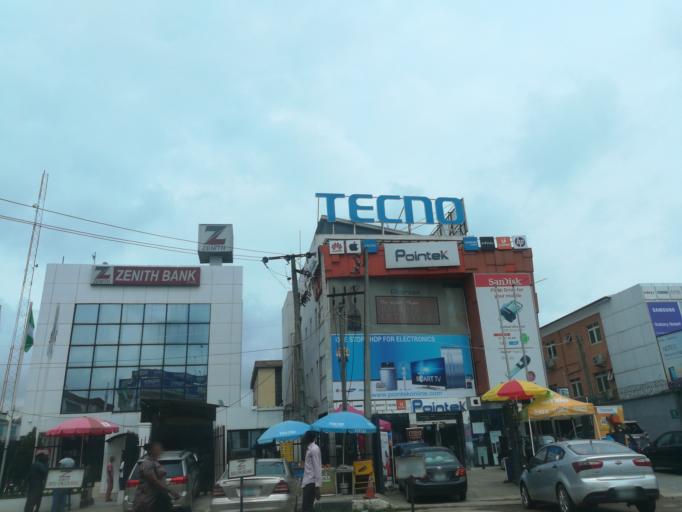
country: NG
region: Lagos
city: Ikeja
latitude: 6.5942
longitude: 3.3385
